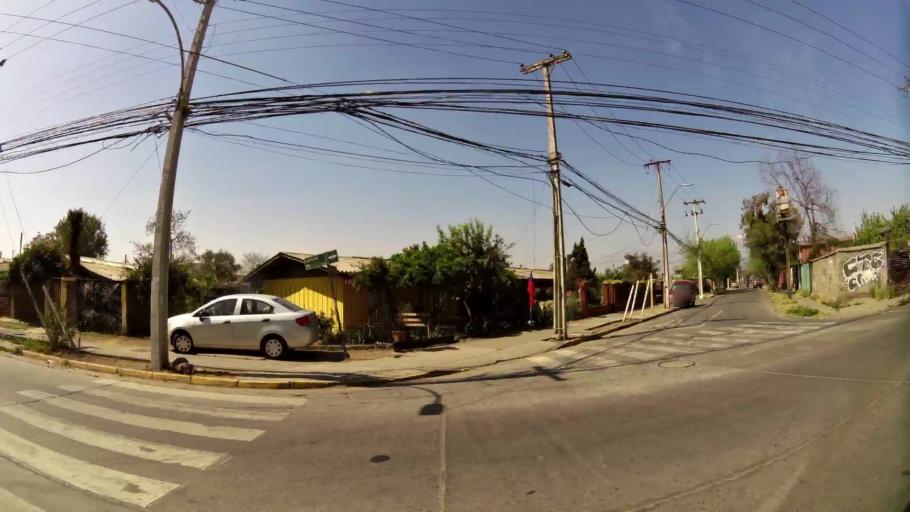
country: CL
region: Santiago Metropolitan
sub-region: Provincia de Santiago
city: Lo Prado
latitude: -33.4053
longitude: -70.7003
